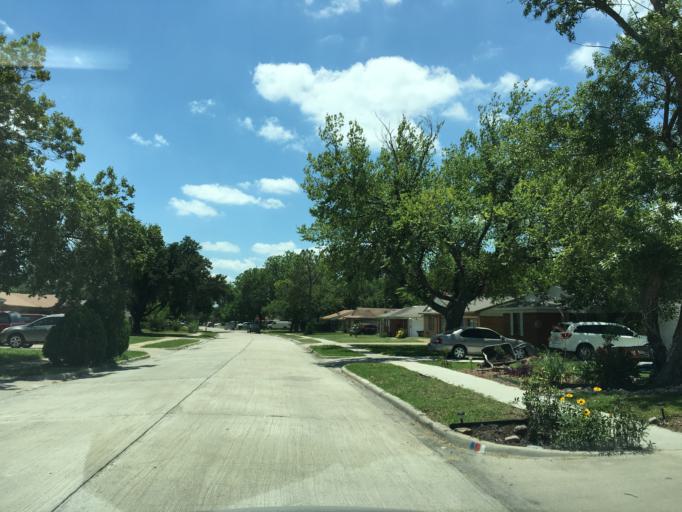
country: US
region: Texas
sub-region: Dallas County
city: Garland
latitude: 32.8323
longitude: -96.6493
